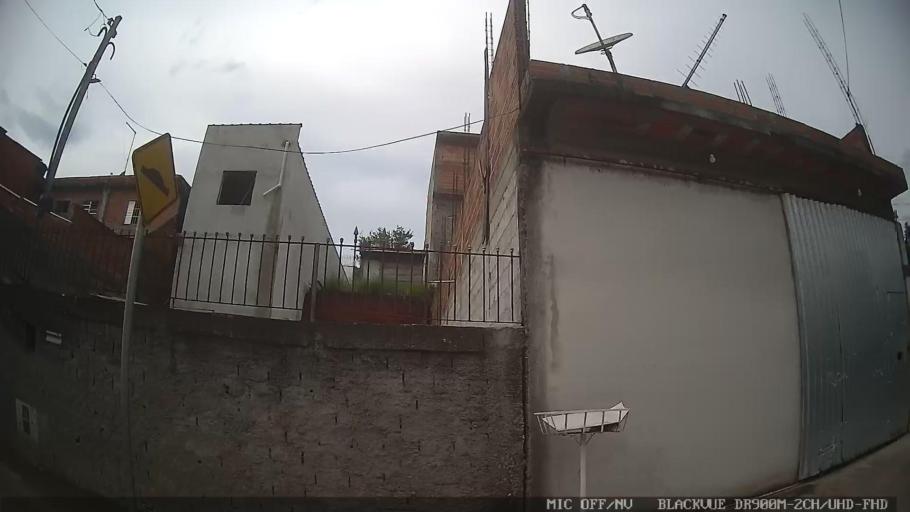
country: BR
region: Sao Paulo
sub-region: Aruja
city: Aruja
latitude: -23.4435
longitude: -46.2796
